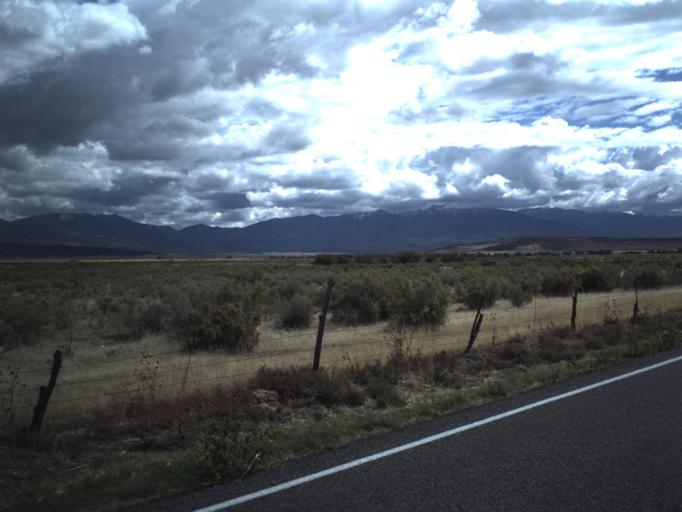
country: US
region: Utah
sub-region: Millard County
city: Fillmore
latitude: 39.0712
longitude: -112.4098
